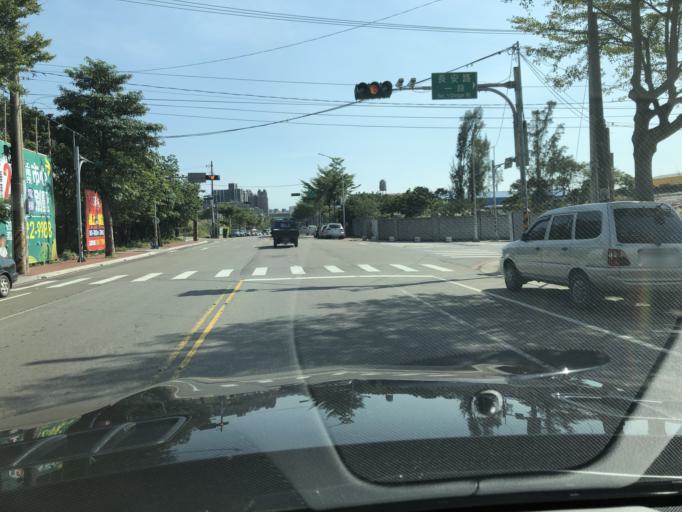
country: TW
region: Taiwan
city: Taoyuan City
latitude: 25.0662
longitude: 121.2908
